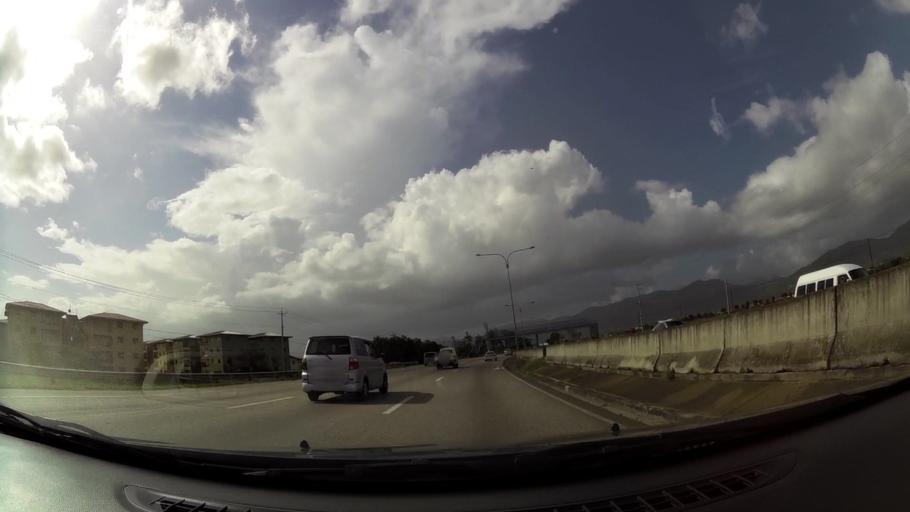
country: TT
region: Tunapuna/Piarco
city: Arouca
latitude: 10.6181
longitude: -61.3510
